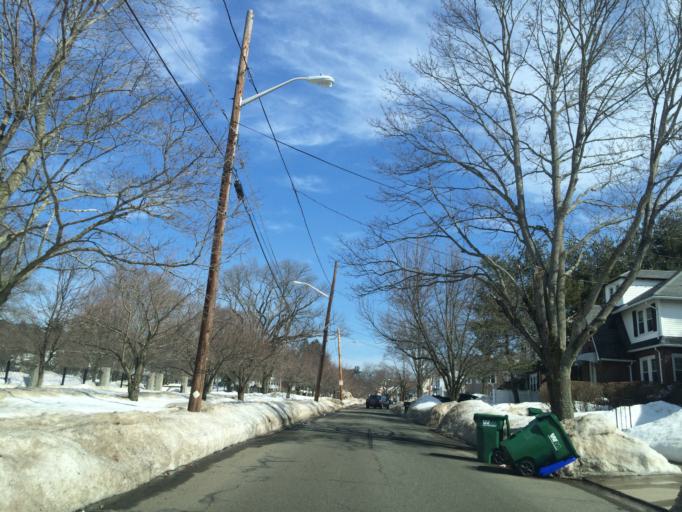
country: US
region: Massachusetts
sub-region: Middlesex County
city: Winchester
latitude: 42.4287
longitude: -71.1335
